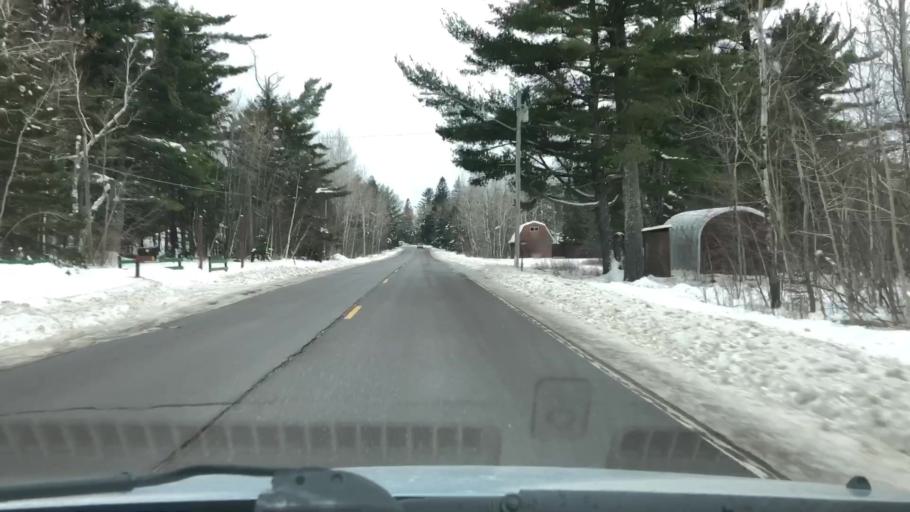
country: US
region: Minnesota
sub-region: Carlton County
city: Carlton
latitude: 46.6648
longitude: -92.4118
